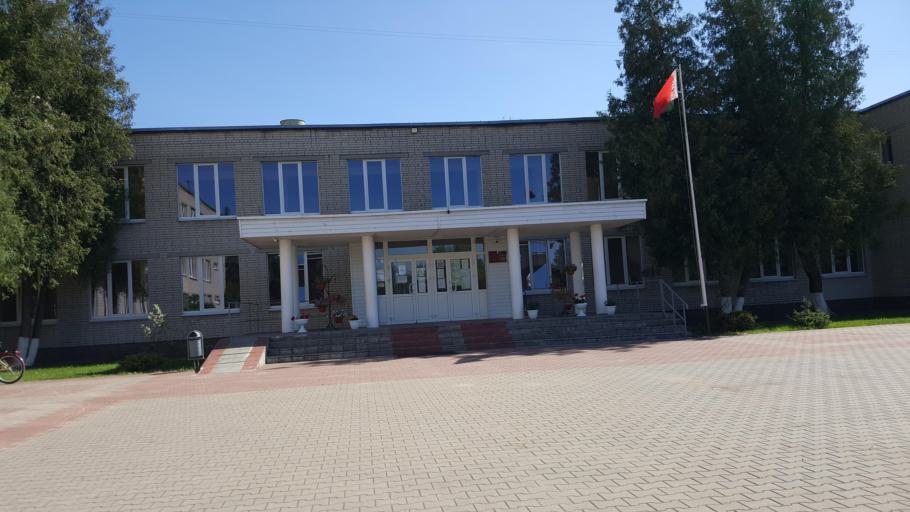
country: BY
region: Brest
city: Charnawchytsy
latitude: 52.2112
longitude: 23.7426
